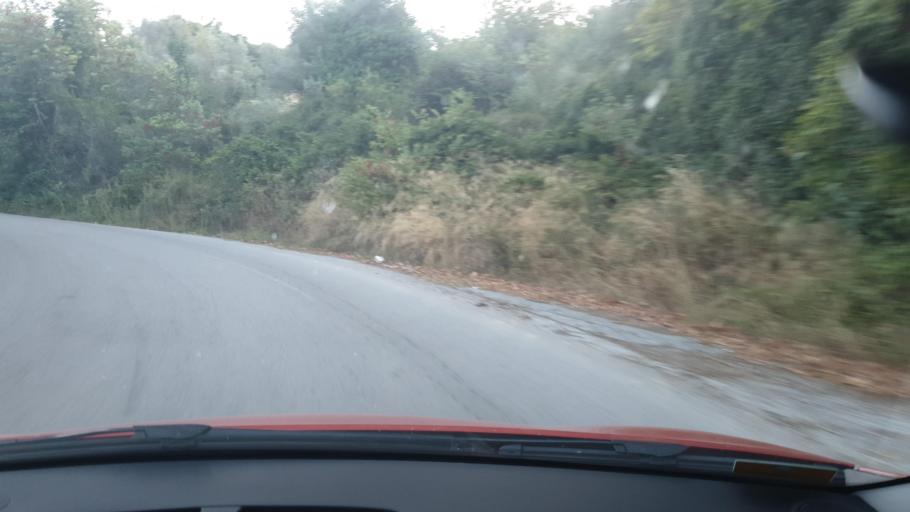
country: GR
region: Central Greece
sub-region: Nomos Evvoias
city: Oxilithos
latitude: 38.5714
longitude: 24.1228
